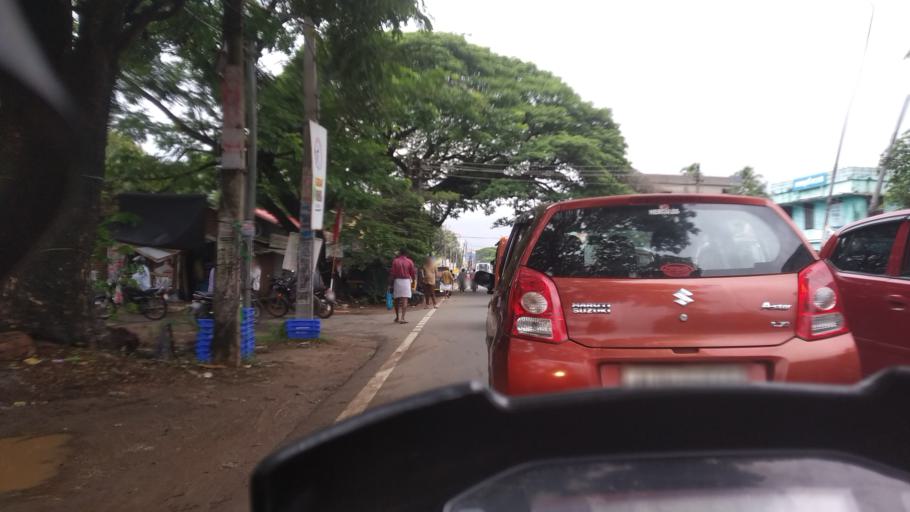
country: IN
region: Kerala
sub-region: Alappuzha
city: Alleppey
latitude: 9.4854
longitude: 76.3376
